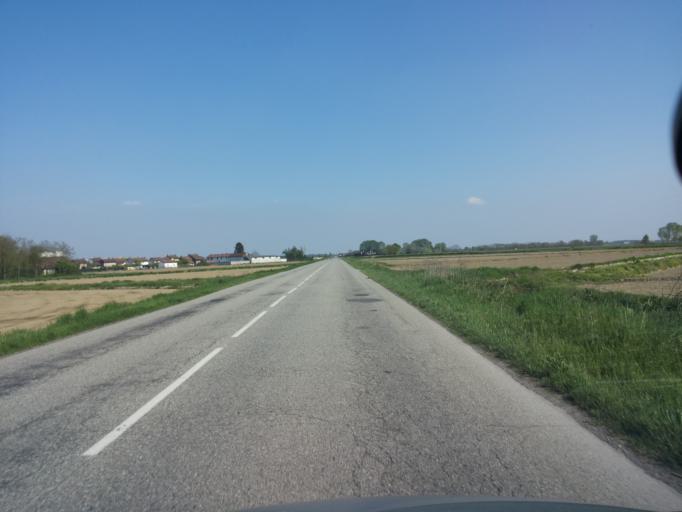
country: IT
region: Lombardy
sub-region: Provincia di Pavia
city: Langosco
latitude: 45.2119
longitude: 8.5623
